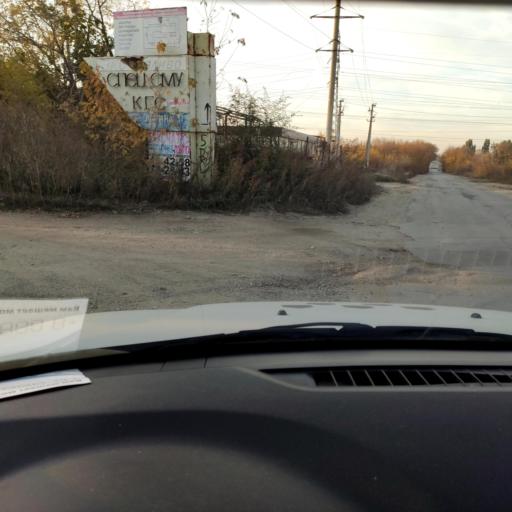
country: RU
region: Samara
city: Tol'yatti
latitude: 53.5290
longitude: 49.4615
